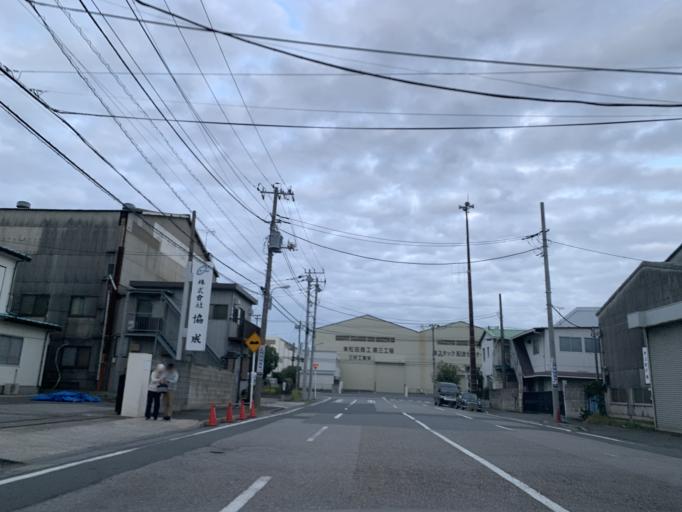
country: JP
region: Tokyo
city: Urayasu
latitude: 35.6311
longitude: 139.8938
